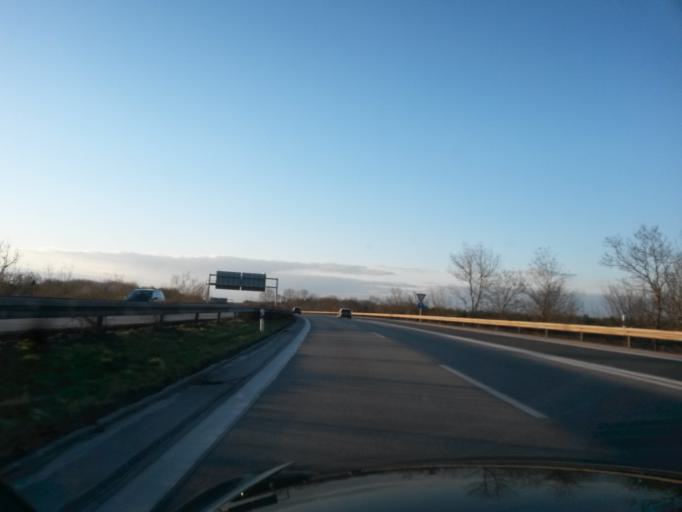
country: DE
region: Bavaria
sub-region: Upper Bavaria
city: Oberschleissheim
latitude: 48.2313
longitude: 11.5426
